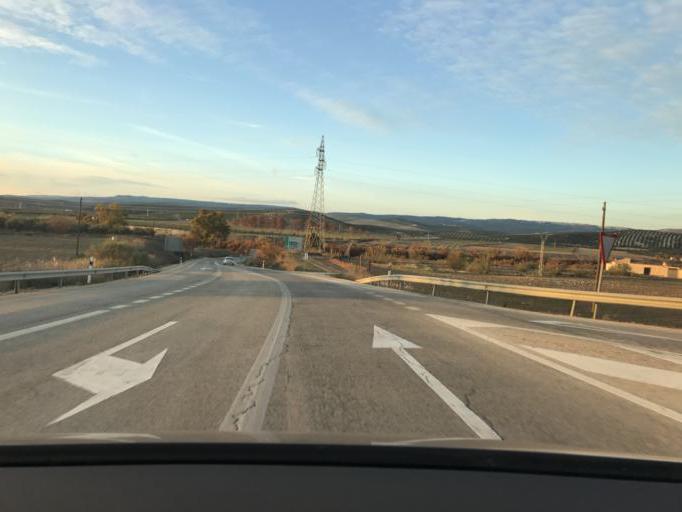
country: ES
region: Andalusia
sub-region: Provincia de Jaen
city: Jodar
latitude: 37.9153
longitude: -3.3476
